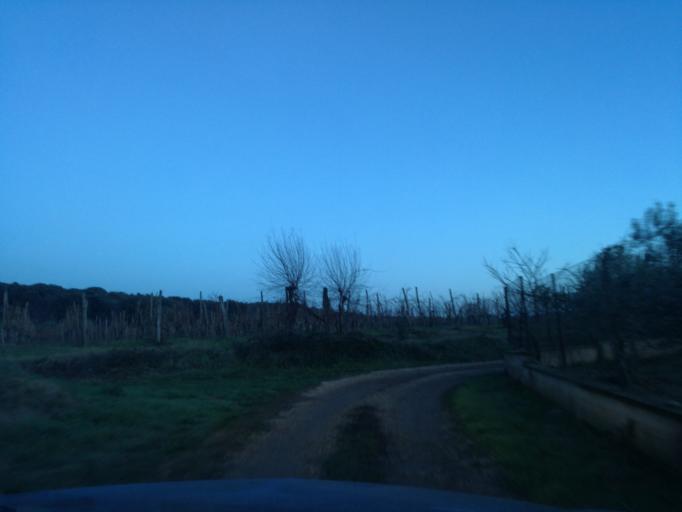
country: HR
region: Istarska
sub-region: Grad Rovinj
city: Rovinj
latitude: 45.1132
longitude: 13.6383
